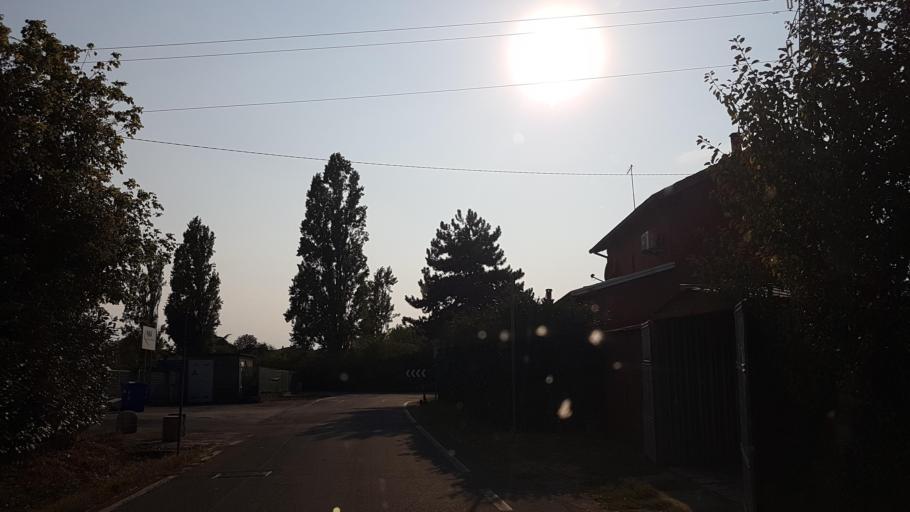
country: IT
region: Emilia-Romagna
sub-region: Provincia di Parma
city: Vicofertile
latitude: 44.7893
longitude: 10.2864
